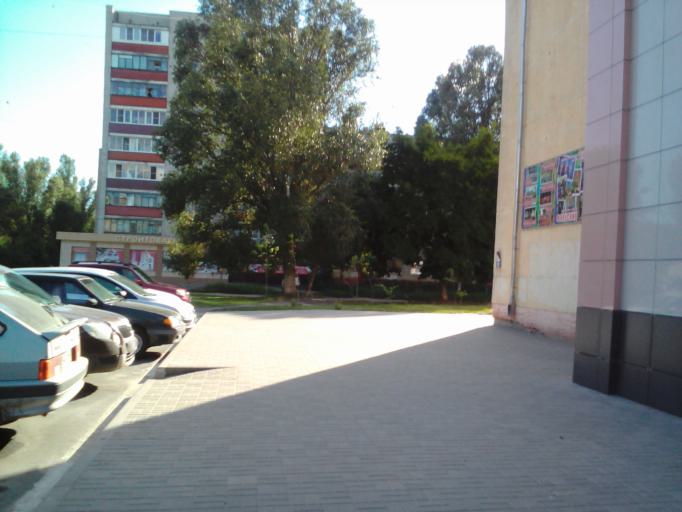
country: RU
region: Kursk
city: Voroshnevo
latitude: 51.6680
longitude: 36.0698
